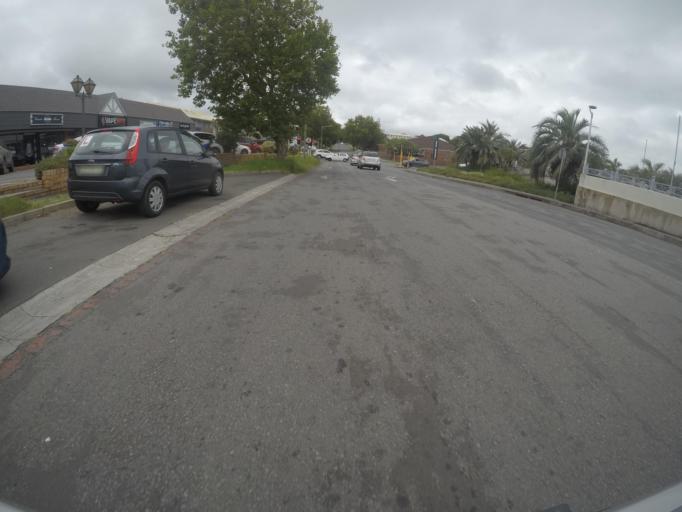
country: ZA
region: Eastern Cape
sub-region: Buffalo City Metropolitan Municipality
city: East London
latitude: -32.9831
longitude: 27.9022
